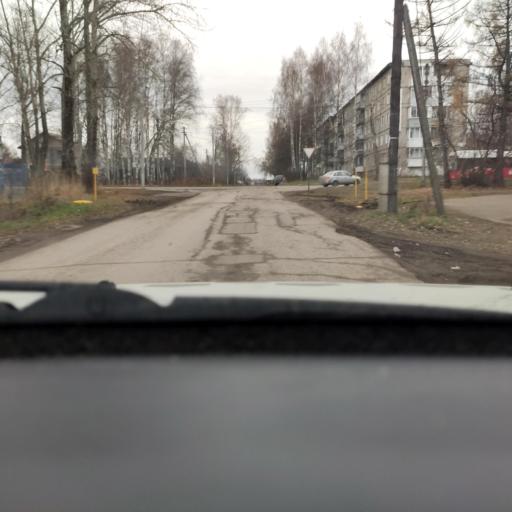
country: RU
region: Perm
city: Polazna
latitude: 58.1286
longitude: 56.3910
